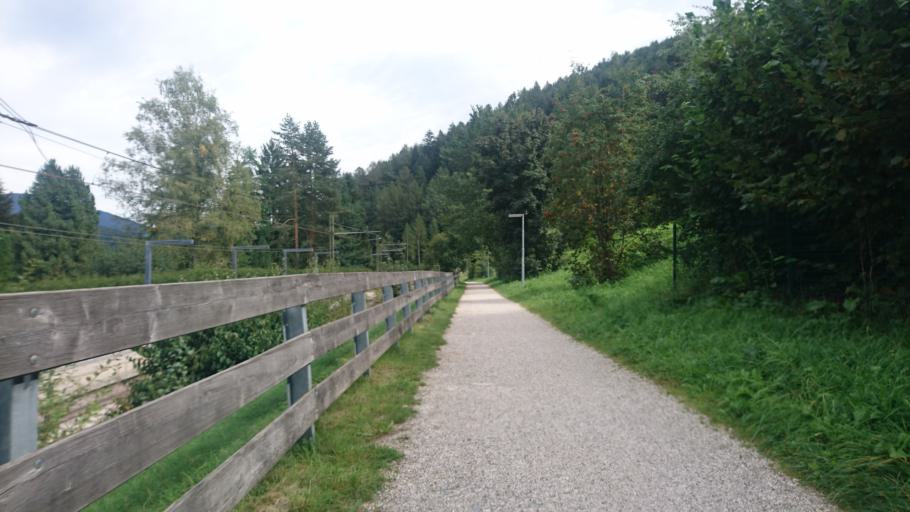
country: IT
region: Trentino-Alto Adige
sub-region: Bolzano
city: San Lorenzo di Sebato
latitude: 46.7814
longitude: 11.9034
